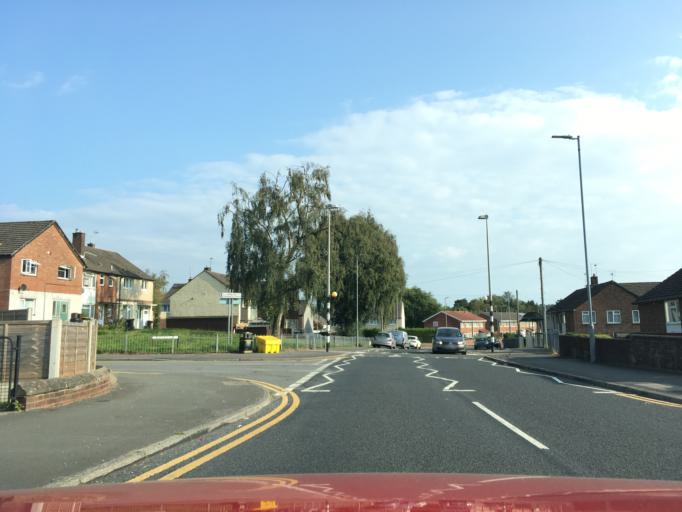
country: GB
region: Wales
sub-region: Newport
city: Newport
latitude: 51.6113
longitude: -3.0199
